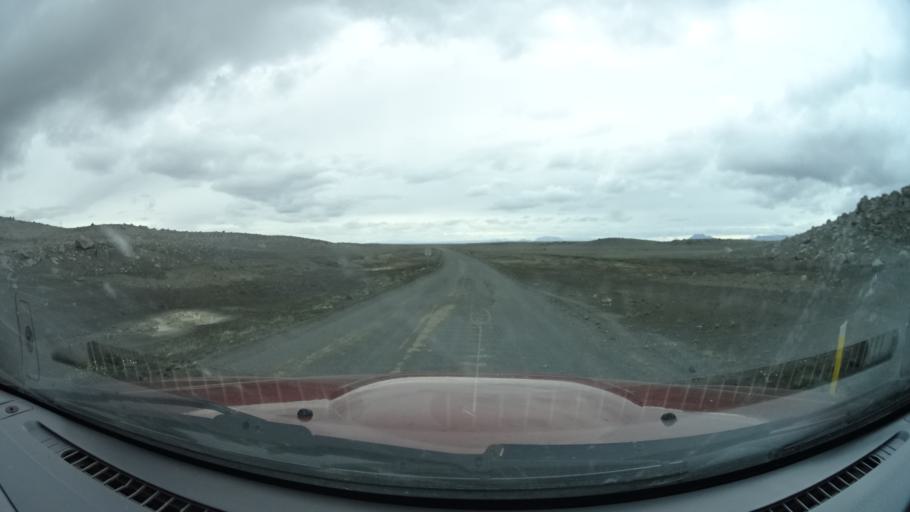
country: IS
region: Northeast
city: Husavik
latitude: 65.8056
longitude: -16.3488
